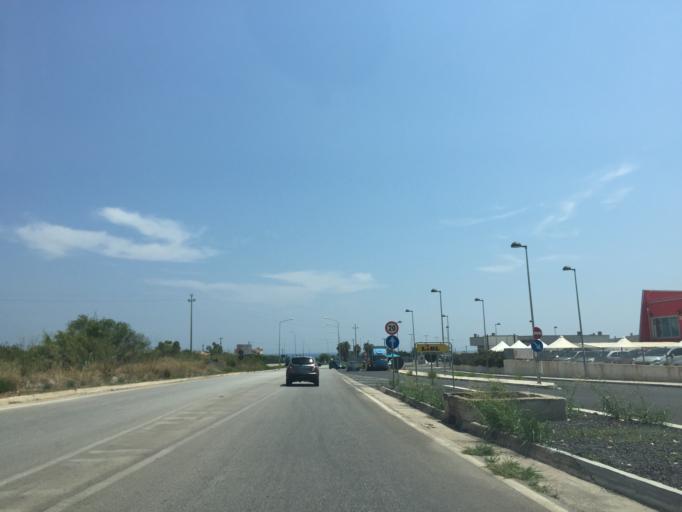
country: IT
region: Sicily
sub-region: Provincia di Siracusa
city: Avola
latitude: 36.9206
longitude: 15.1443
